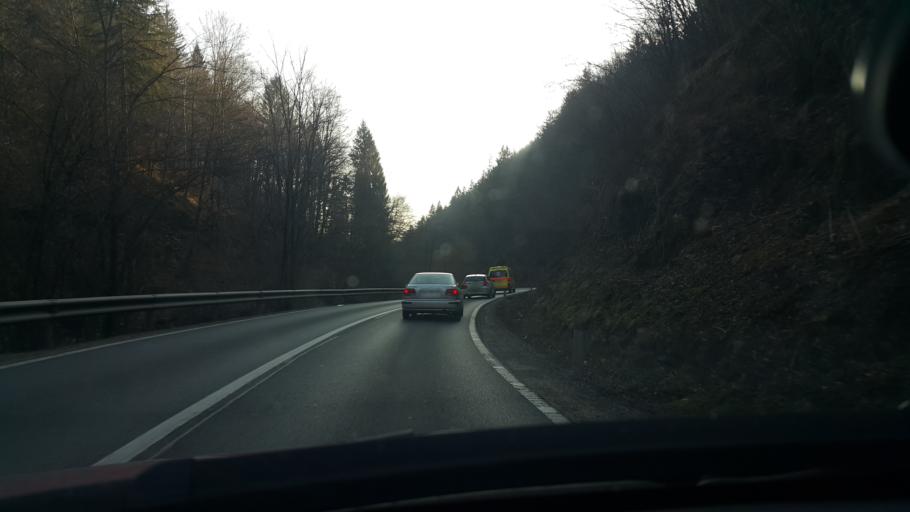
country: SI
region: Zalec
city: Gotovlje
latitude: 46.3122
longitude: 15.1744
